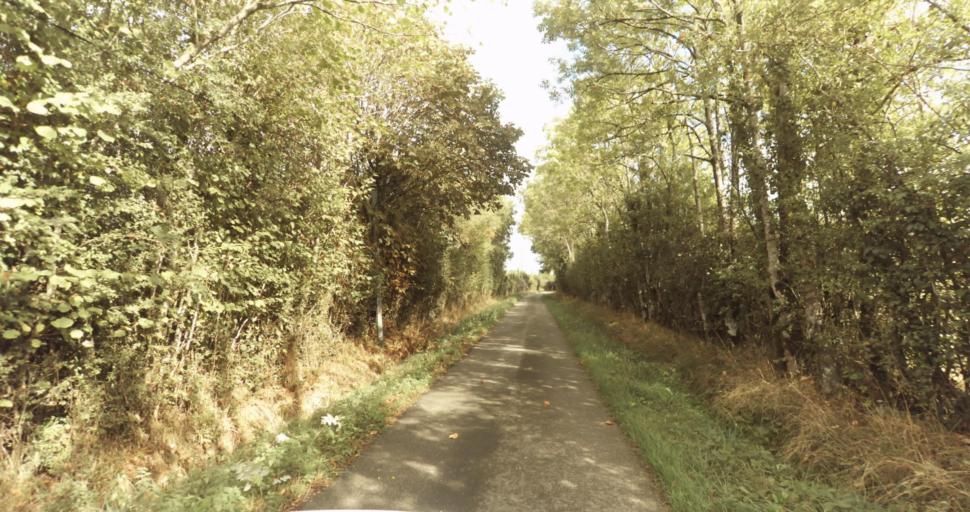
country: FR
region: Lower Normandy
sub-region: Departement de l'Orne
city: Gace
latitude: 48.8377
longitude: 0.3602
